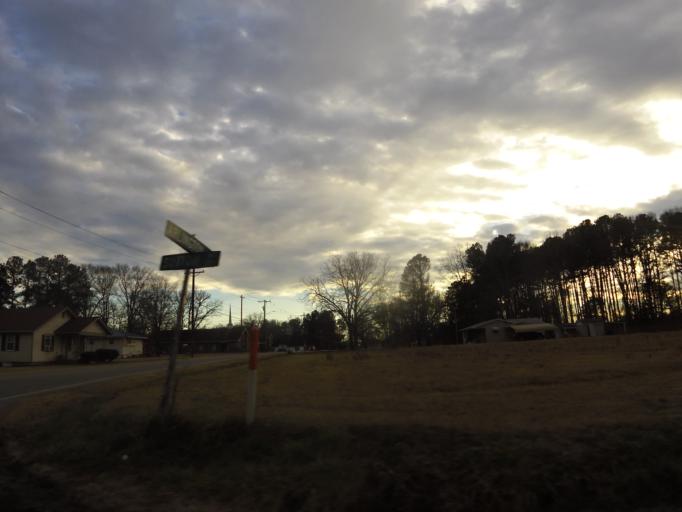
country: US
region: North Carolina
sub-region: Nash County
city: Rocky Mount
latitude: 35.9159
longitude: -77.8026
